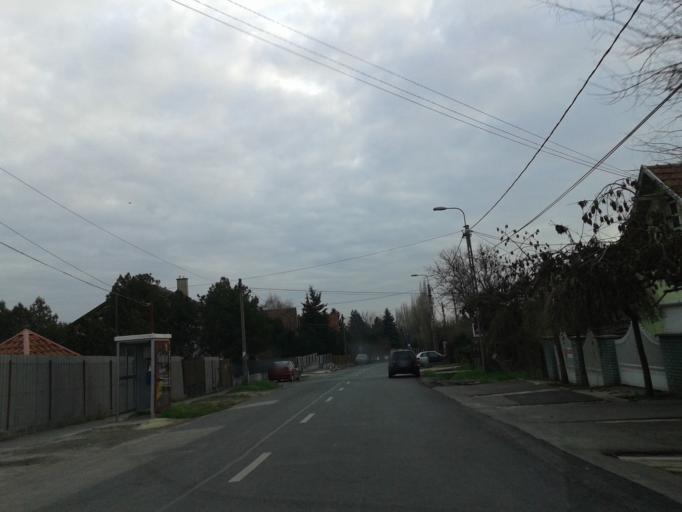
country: HU
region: Pest
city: Diosd
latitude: 47.4037
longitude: 18.9914
